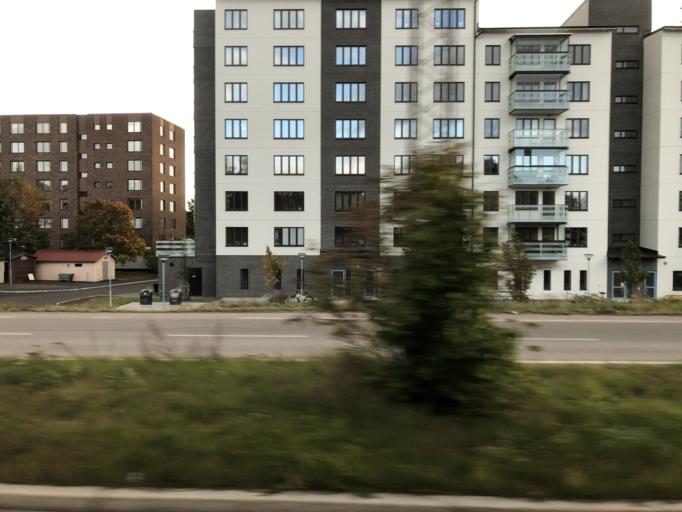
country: SE
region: Stockholm
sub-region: Jarfalla Kommun
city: Jakobsberg
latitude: 59.4254
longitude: 17.8253
